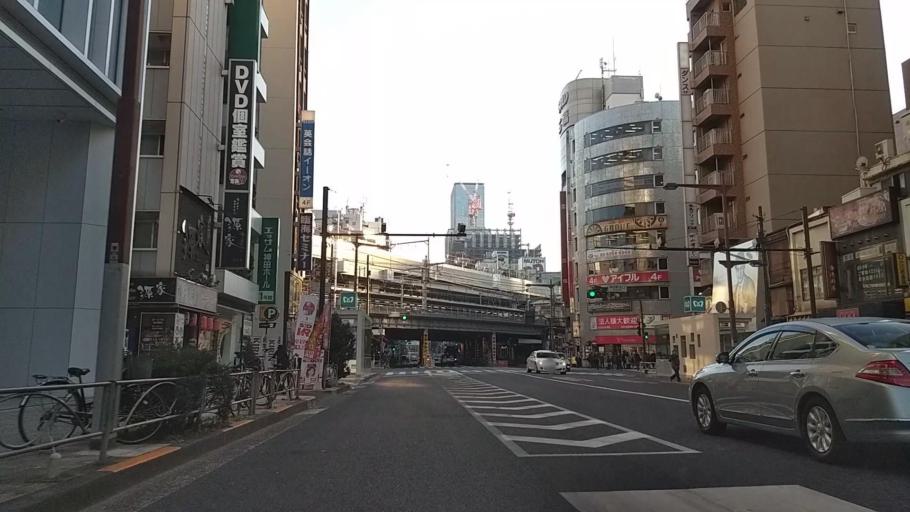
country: JP
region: Tokyo
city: Tokyo
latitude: 35.6937
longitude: 139.7709
